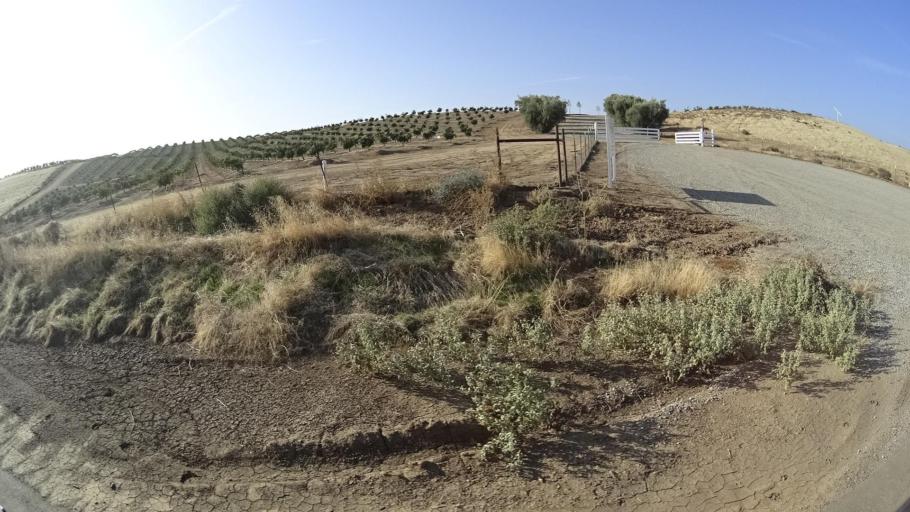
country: US
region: California
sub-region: Tulare County
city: Richgrove
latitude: 35.6436
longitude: -119.0506
